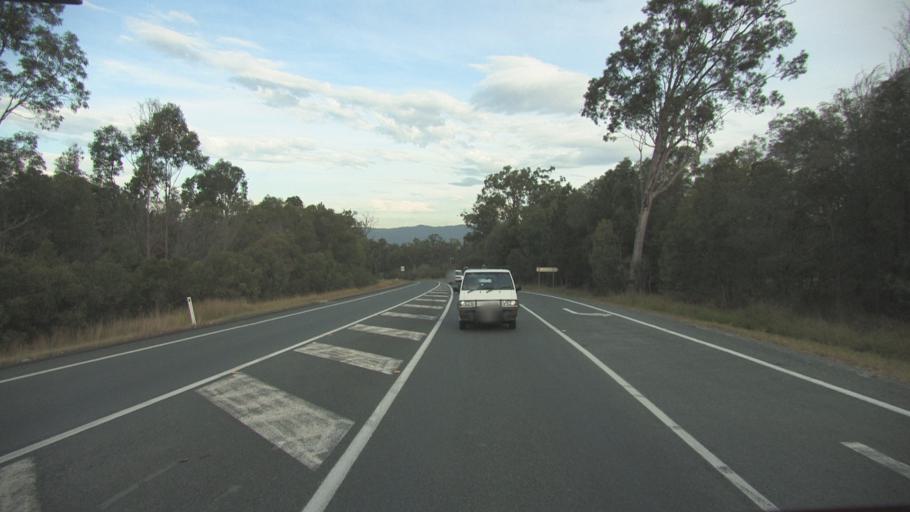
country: AU
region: Queensland
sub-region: Logan
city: Chambers Flat
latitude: -27.8361
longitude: 153.1081
